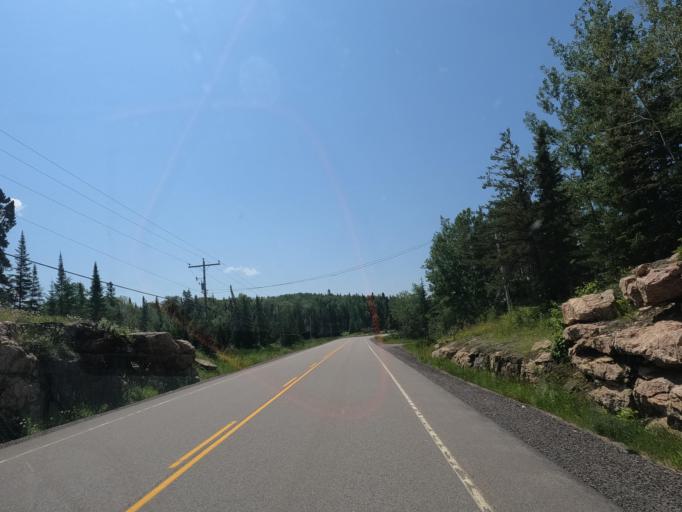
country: CA
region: Ontario
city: Dryden
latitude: 49.8666
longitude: -93.3593
